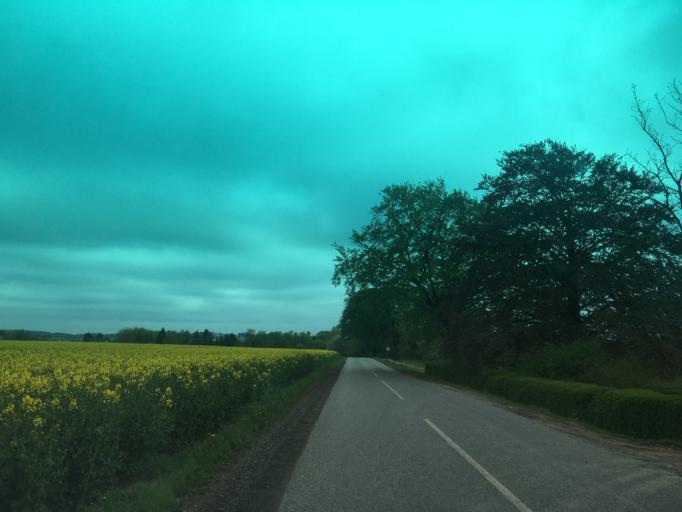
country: DK
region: Zealand
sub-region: Ringsted Kommune
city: Ringsted
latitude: 55.4161
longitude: 11.7072
